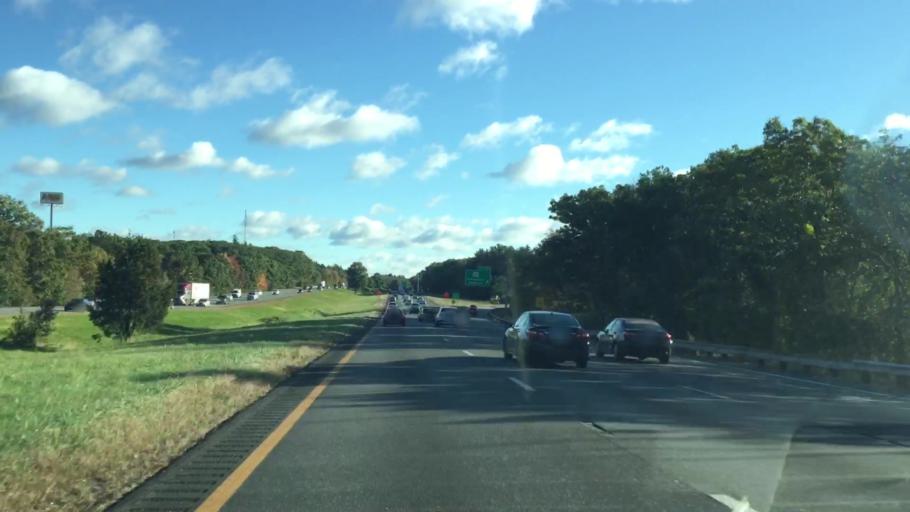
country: US
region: Massachusetts
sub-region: Middlesex County
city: Tewksbury
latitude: 42.6397
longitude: -71.2376
